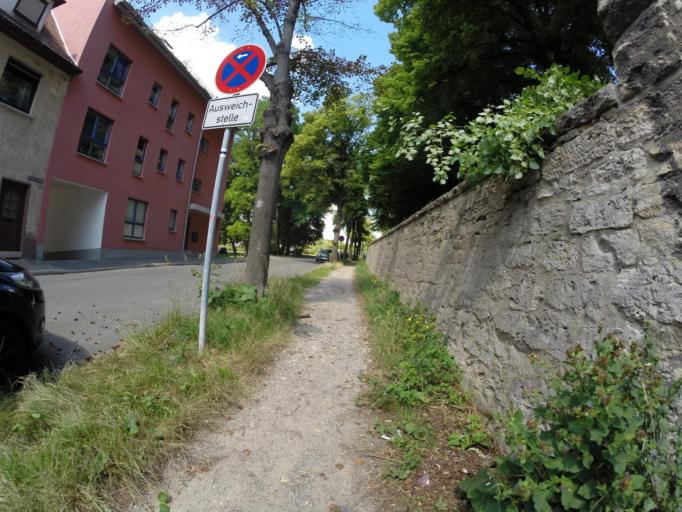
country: DE
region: Thuringia
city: Jena
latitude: 50.9331
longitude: 11.6051
